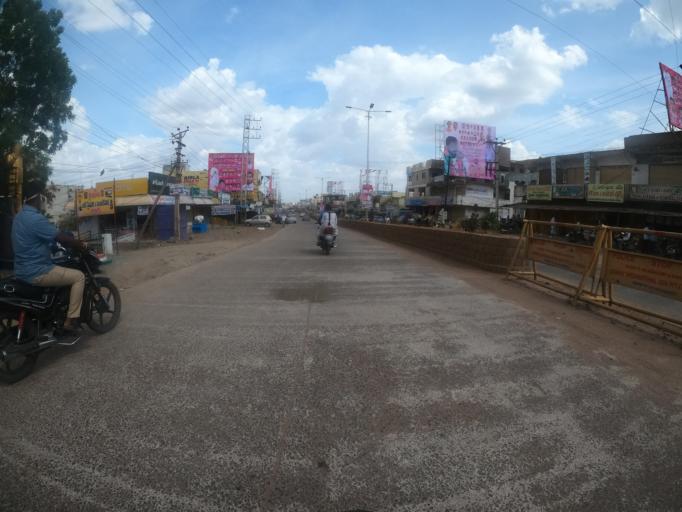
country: IN
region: Telangana
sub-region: Rangareddi
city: Sriramnagar
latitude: 17.3134
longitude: 78.1394
